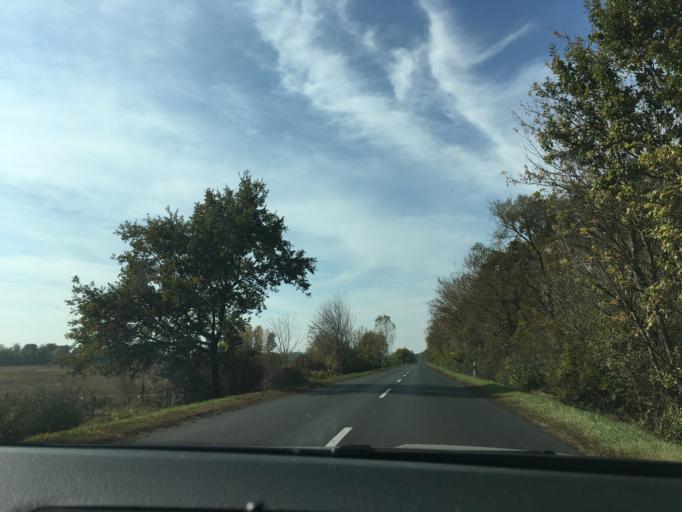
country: HU
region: Hajdu-Bihar
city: Vamospercs
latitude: 47.5284
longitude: 21.8435
